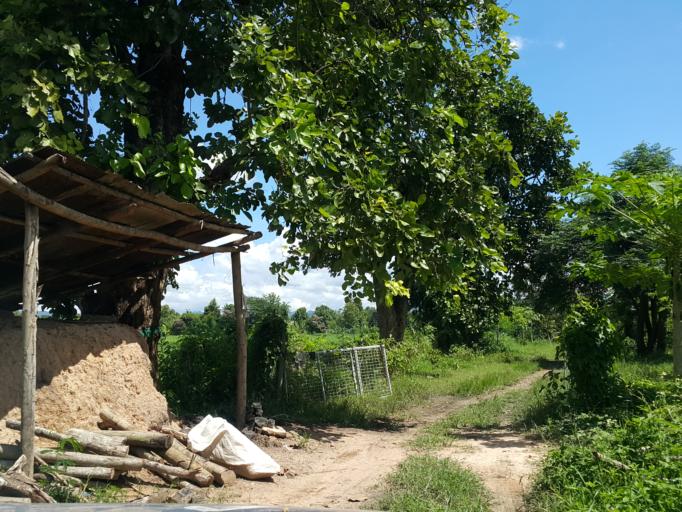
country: TH
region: Chiang Mai
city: San Kamphaeng
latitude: 18.7641
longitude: 99.1229
